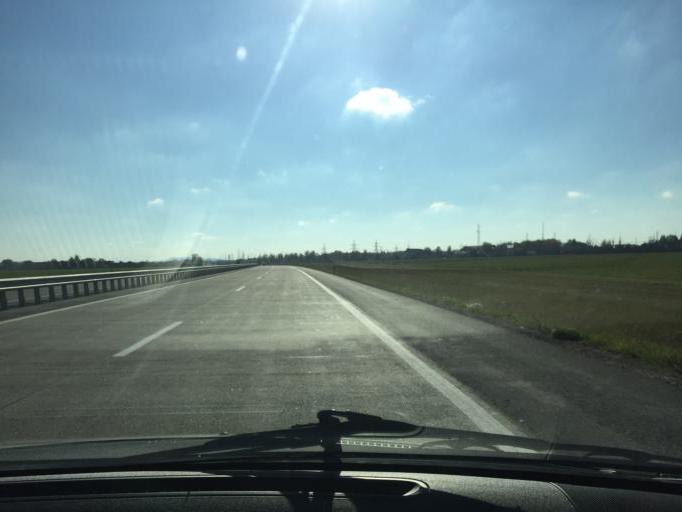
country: BY
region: Minsk
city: Slutsk
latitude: 53.0266
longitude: 27.4843
